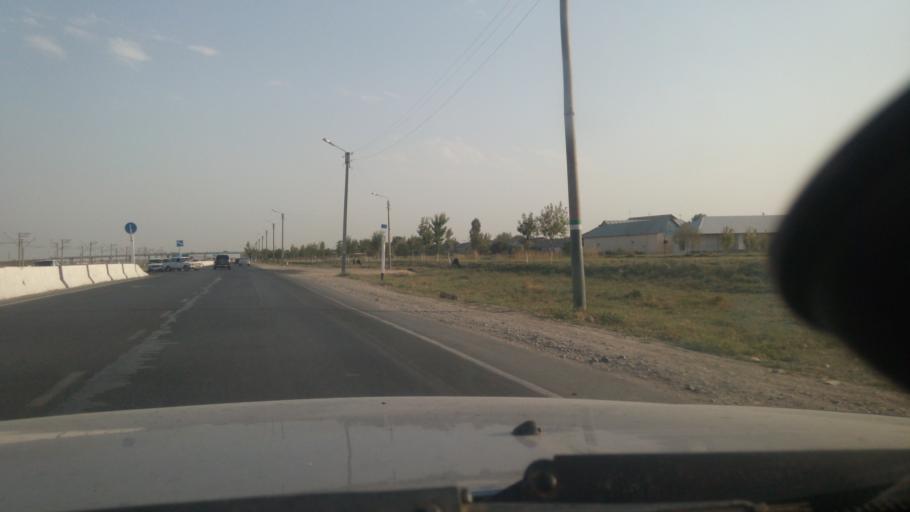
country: UZ
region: Sirdaryo
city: Guliston
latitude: 40.4817
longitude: 68.7683
